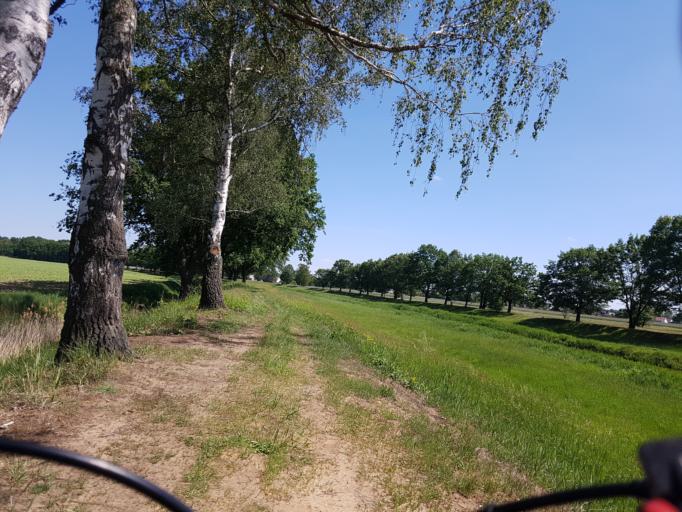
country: DE
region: Brandenburg
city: Elsterwerda
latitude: 51.4551
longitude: 13.4988
